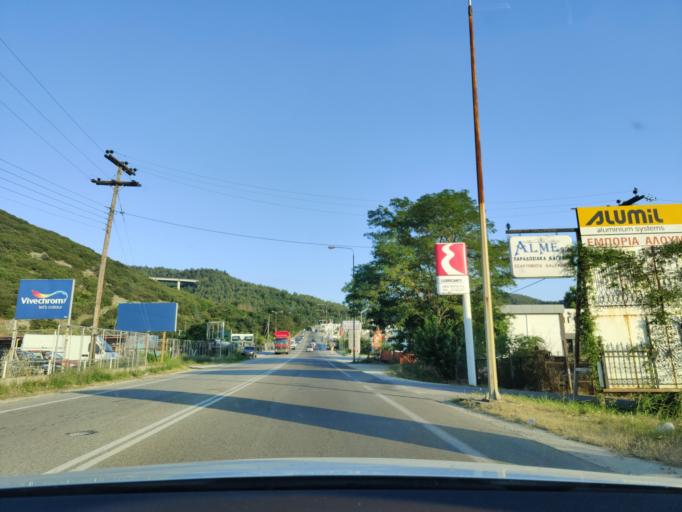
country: GR
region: East Macedonia and Thrace
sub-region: Nomos Kavalas
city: Amygdaleonas
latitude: 40.9553
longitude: 24.3658
